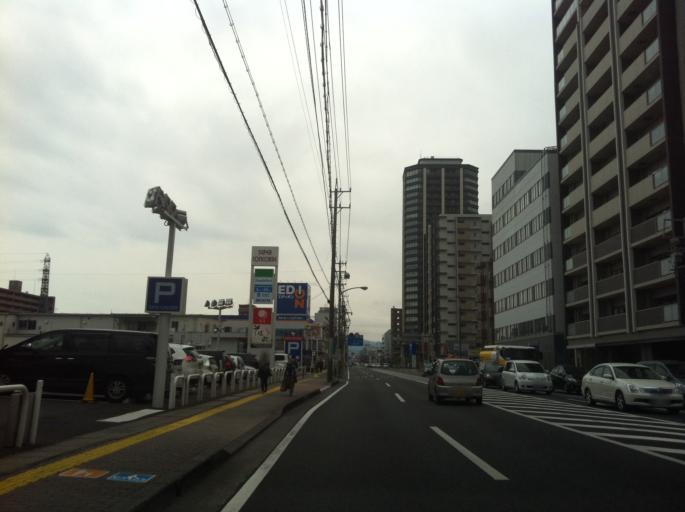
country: JP
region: Shizuoka
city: Shizuoka-shi
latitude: 34.9829
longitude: 138.4159
